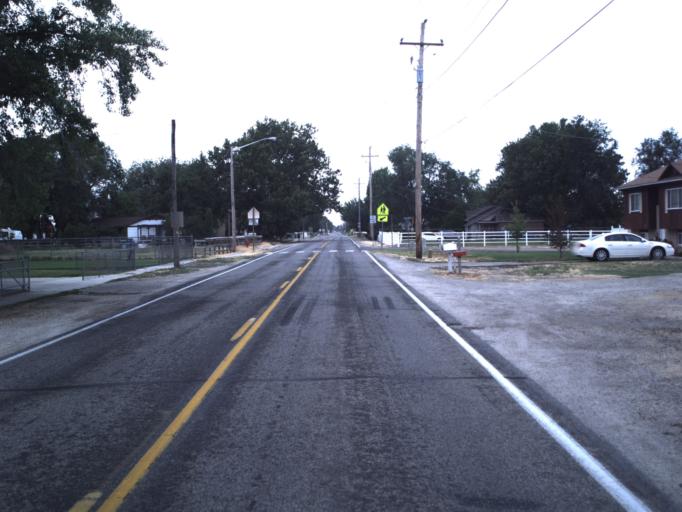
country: US
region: Utah
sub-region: Davis County
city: West Point
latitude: 41.1223
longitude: -112.1126
